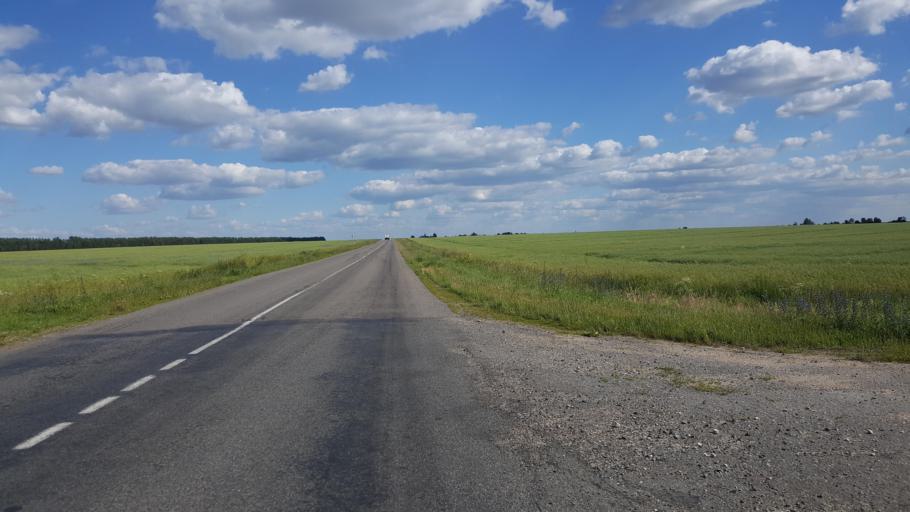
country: BY
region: Brest
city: Kamyanyets
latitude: 52.4599
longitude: 23.7217
